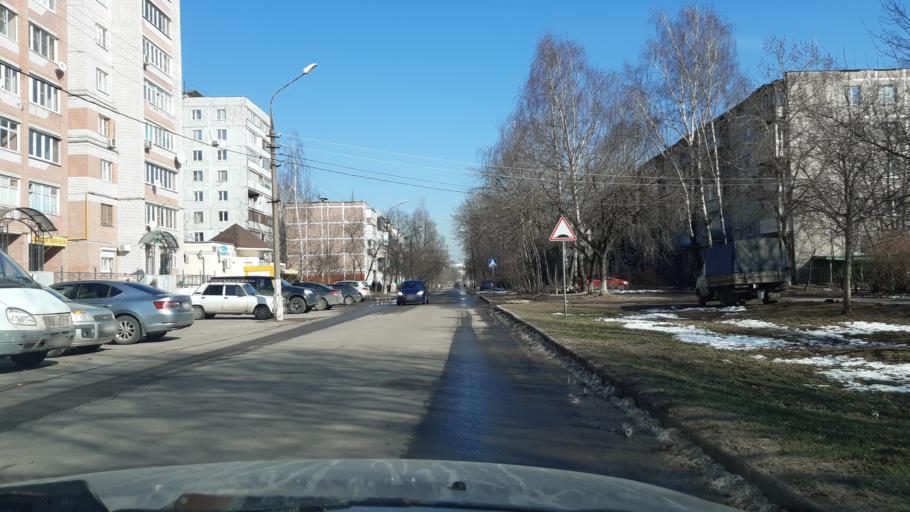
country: RU
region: Moskovskaya
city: Elektrostal'
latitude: 55.7703
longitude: 38.4217
